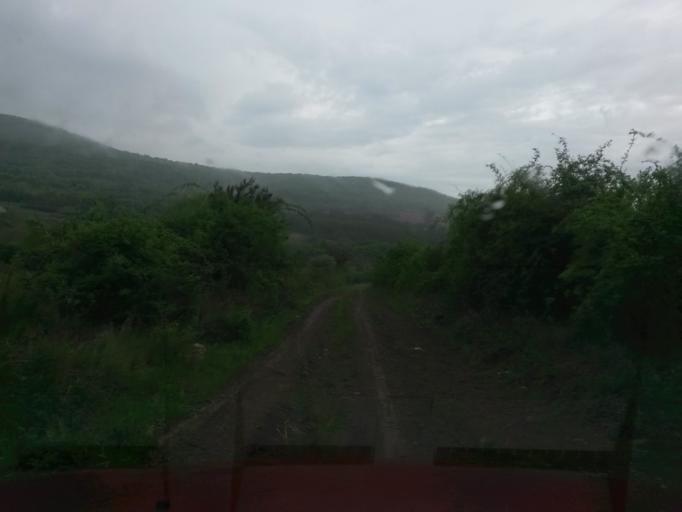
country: HU
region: Borsod-Abauj-Zemplen
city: Gonc
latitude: 48.5101
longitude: 21.3295
